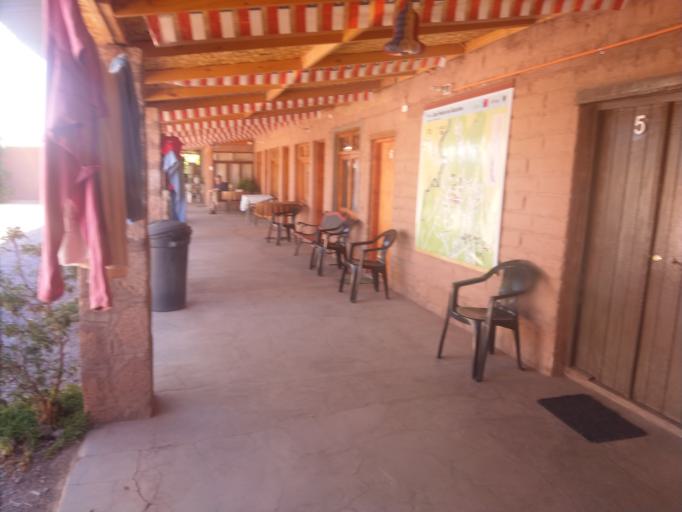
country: CL
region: Antofagasta
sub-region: Provincia de El Loa
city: San Pedro de Atacama
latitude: -22.9140
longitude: -68.2026
